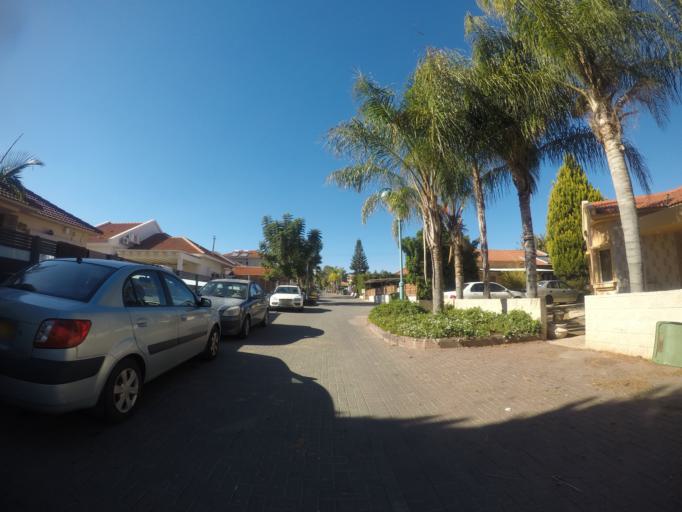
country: IL
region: Southern District
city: Qiryat Gat
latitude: 31.6226
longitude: 34.7090
